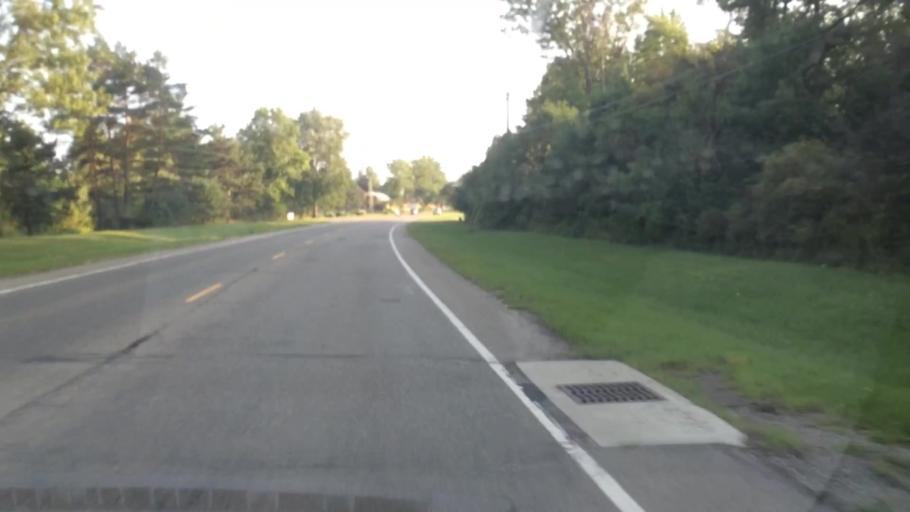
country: US
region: Ohio
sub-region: Summit County
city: Boston Heights
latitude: 41.2147
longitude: -81.4913
